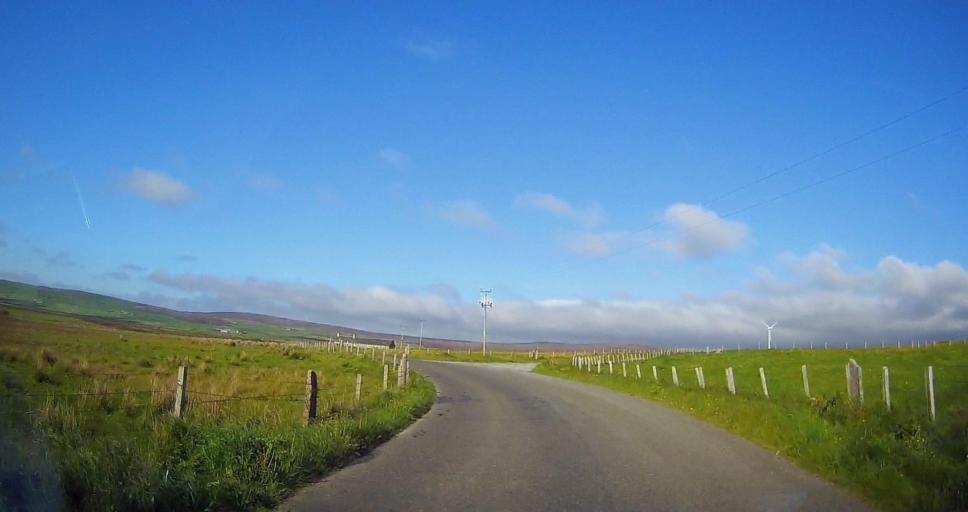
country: GB
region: Scotland
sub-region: Orkney Islands
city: Stromness
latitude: 59.0746
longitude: -3.2058
